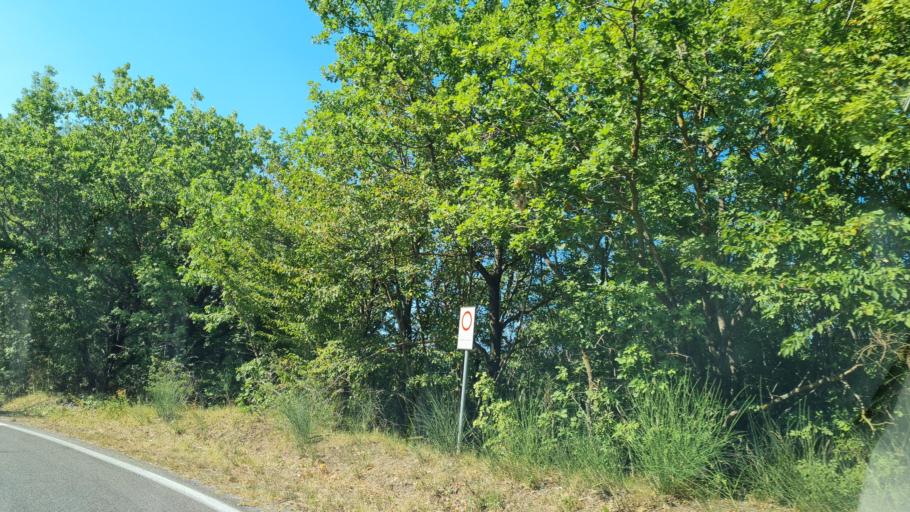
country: IT
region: Tuscany
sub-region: Provincia di Siena
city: Chianciano Terme
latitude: 43.0387
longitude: 11.7978
